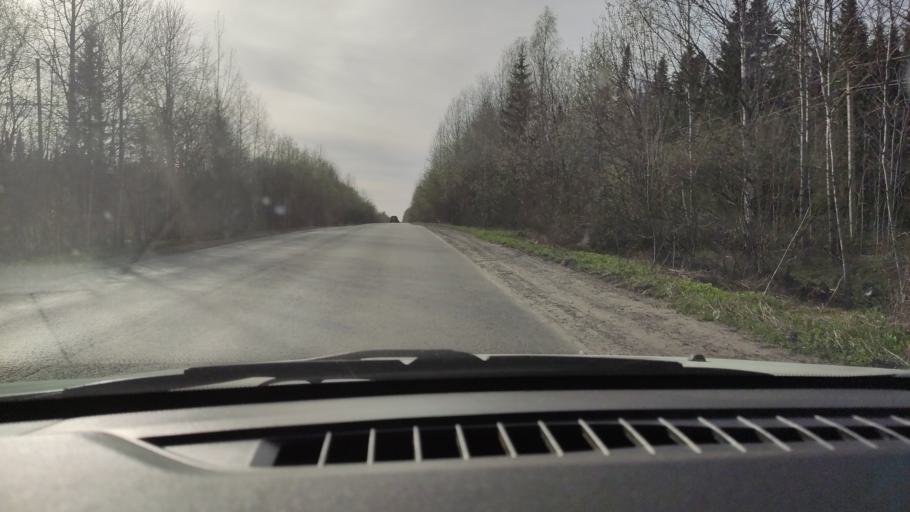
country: RU
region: Perm
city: Ferma
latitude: 57.9389
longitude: 56.4530
